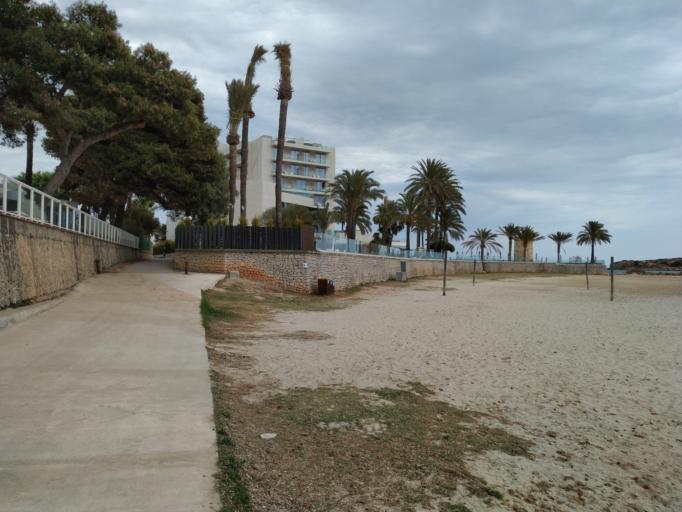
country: ES
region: Balearic Islands
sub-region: Illes Balears
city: Ibiza
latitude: 38.8970
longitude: 1.4159
